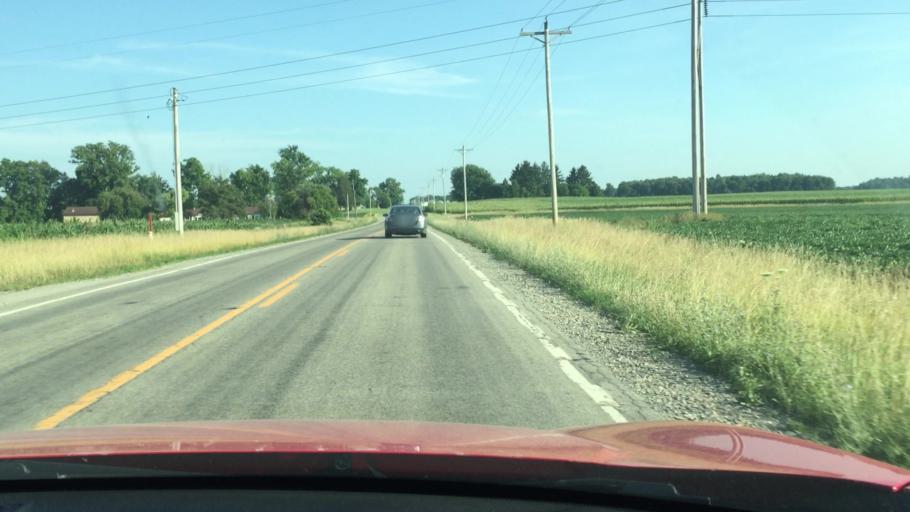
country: US
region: Ohio
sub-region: Hardin County
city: Ada
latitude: 40.6691
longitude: -83.8544
